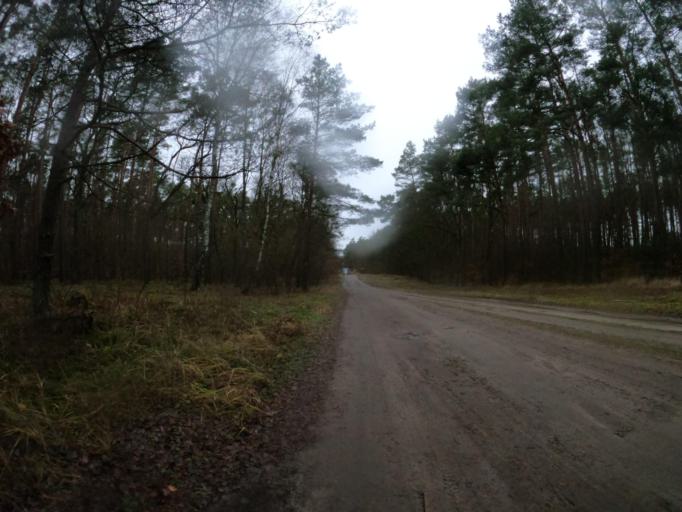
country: PL
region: West Pomeranian Voivodeship
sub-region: Powiat mysliborski
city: Debno
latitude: 52.7990
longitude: 14.7529
